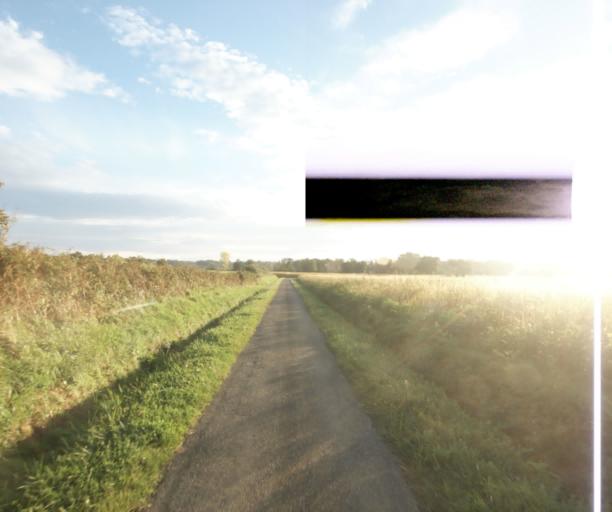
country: FR
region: Midi-Pyrenees
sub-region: Departement du Gers
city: Le Houga
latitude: 43.8292
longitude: -0.1112
